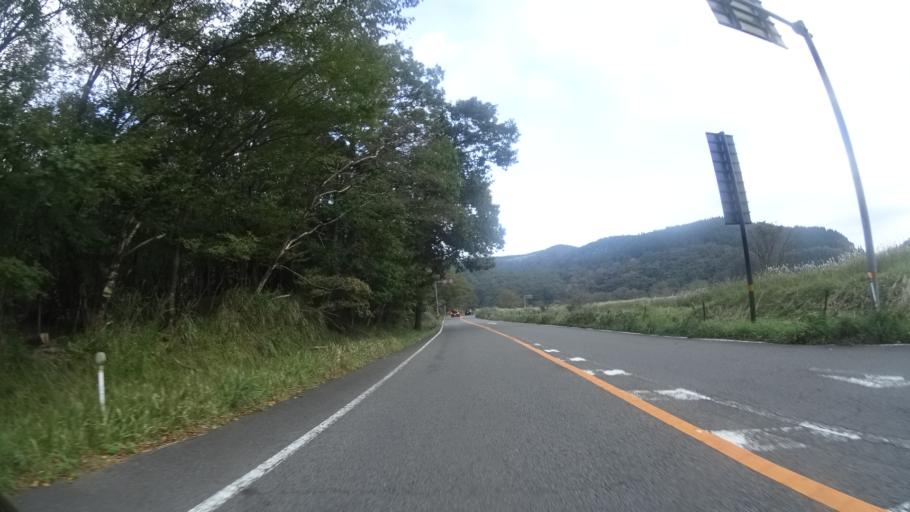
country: JP
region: Oita
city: Beppu
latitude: 33.2749
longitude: 131.4130
